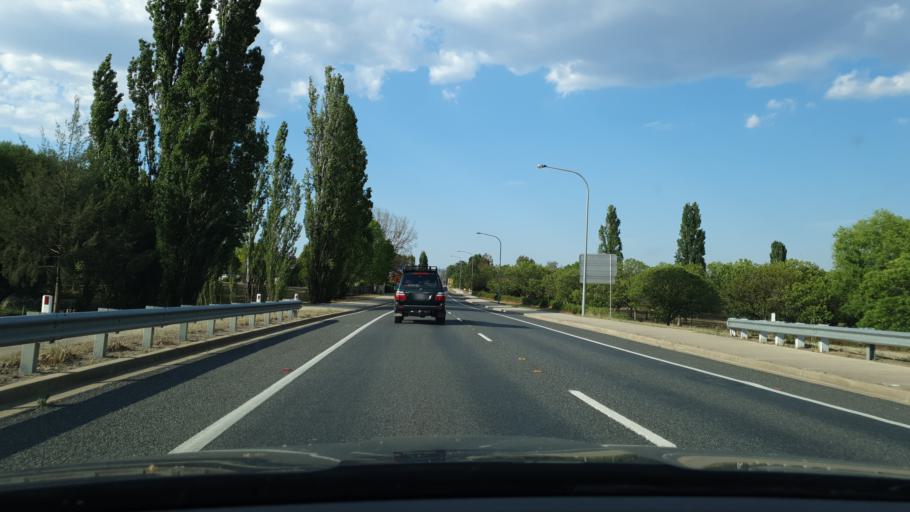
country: AU
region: New South Wales
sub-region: Tenterfield Municipality
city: Carrolls Creek
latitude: -29.0441
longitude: 152.0209
